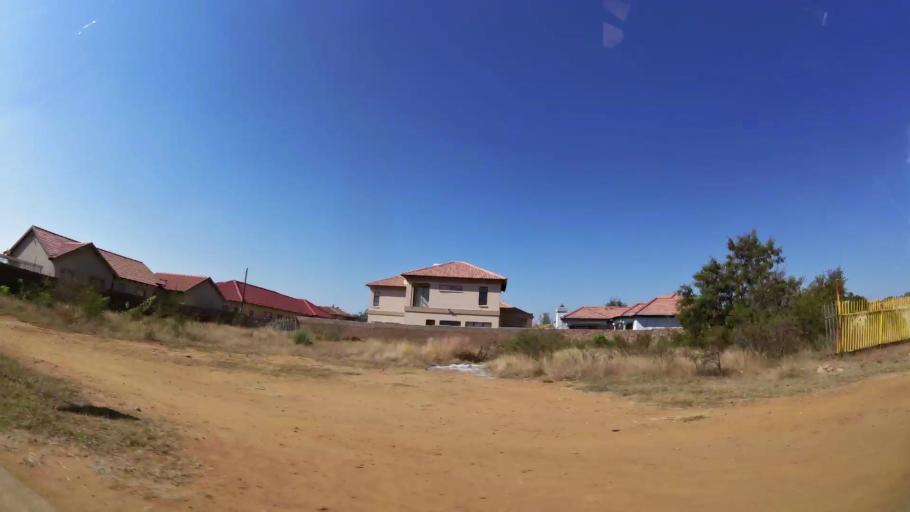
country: ZA
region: Gauteng
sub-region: City of Tshwane Metropolitan Municipality
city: Pretoria
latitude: -25.6517
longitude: 28.2631
